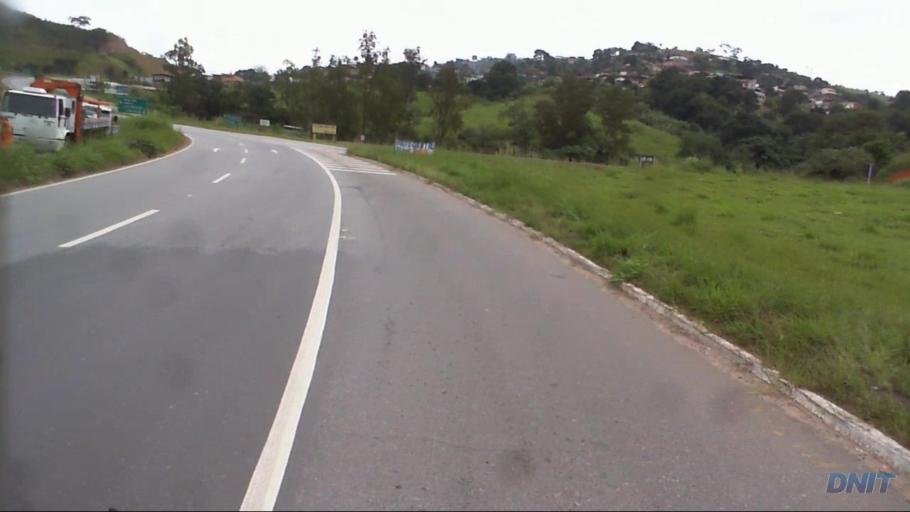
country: BR
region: Minas Gerais
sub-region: Nova Era
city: Nova Era
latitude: -19.7530
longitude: -43.0272
